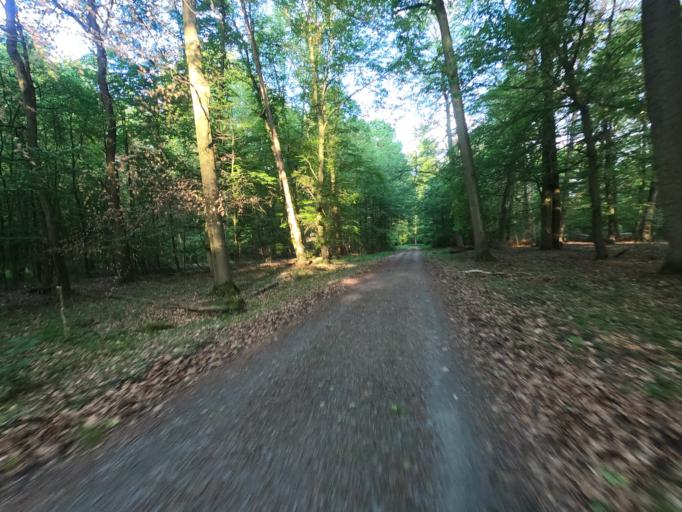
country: DE
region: Hesse
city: Morfelden-Walldorf
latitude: 49.9762
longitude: 8.5405
